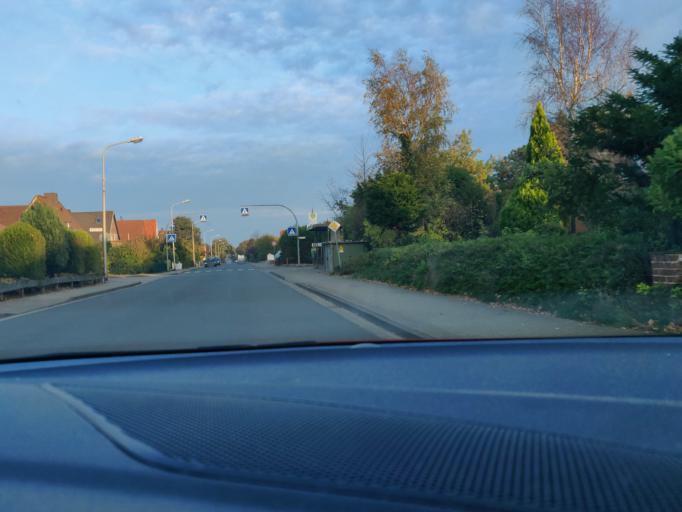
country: DE
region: Lower Saxony
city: Cuxhaven
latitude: 53.8615
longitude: 8.6126
